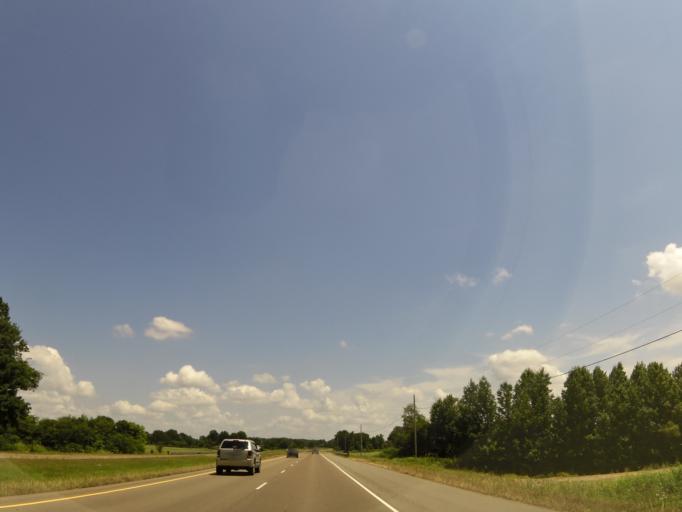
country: US
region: Tennessee
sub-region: Crockett County
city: Alamo
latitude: 35.8561
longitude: -89.2013
